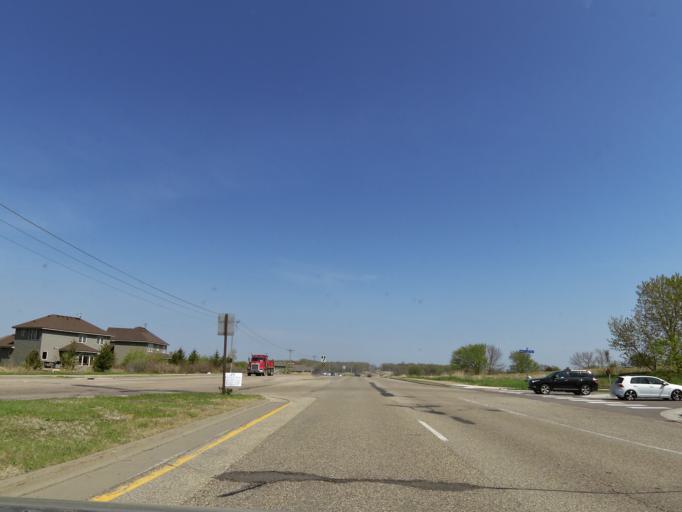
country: US
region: Minnesota
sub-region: Scott County
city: Prior Lake
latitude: 44.7391
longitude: -93.4397
